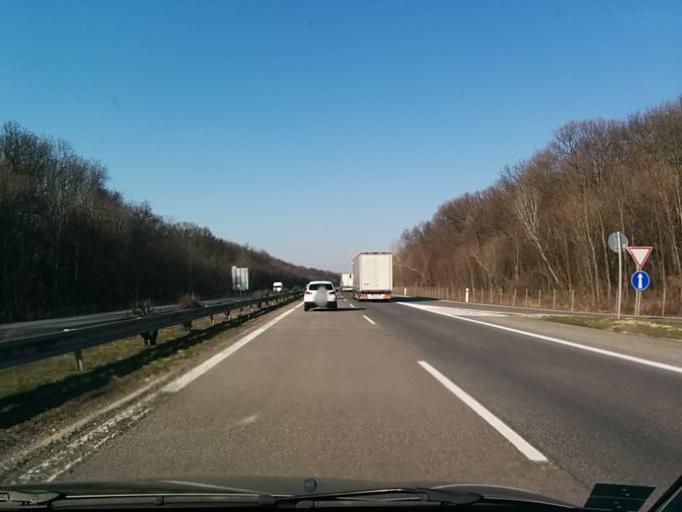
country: SK
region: Trnavsky
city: Leopoldov
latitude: 48.4664
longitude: 17.7414
